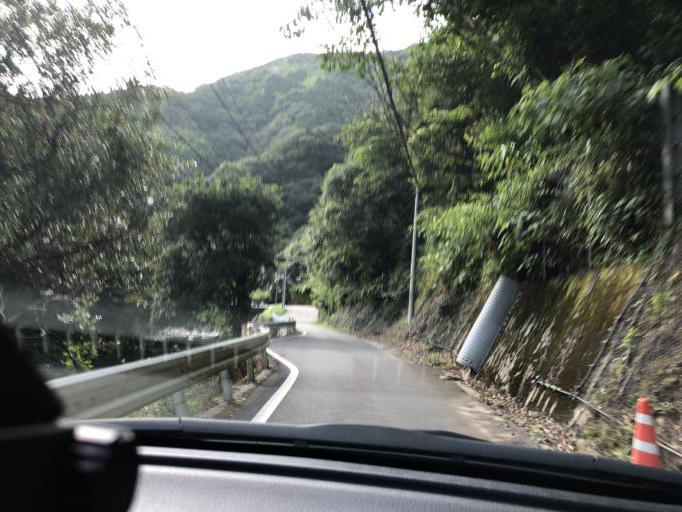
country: JP
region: Kochi
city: Kochi-shi
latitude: 33.6284
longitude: 133.5088
